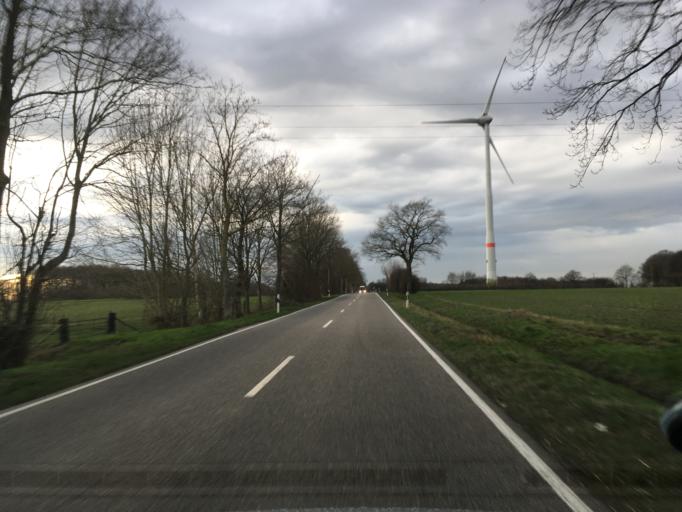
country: DE
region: North Rhine-Westphalia
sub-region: Regierungsbezirk Munster
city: Schoppingen
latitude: 52.0669
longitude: 7.1843
